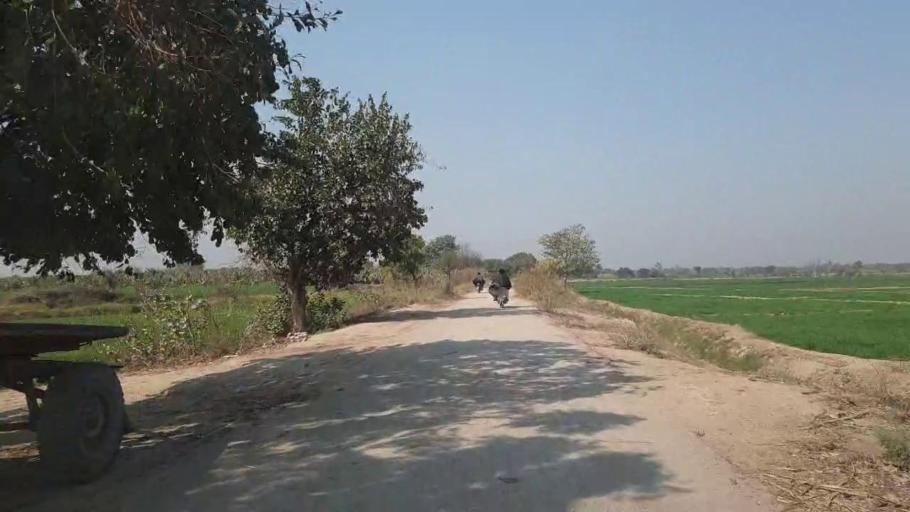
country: PK
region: Sindh
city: Tando Jam
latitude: 25.3284
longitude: 68.6048
